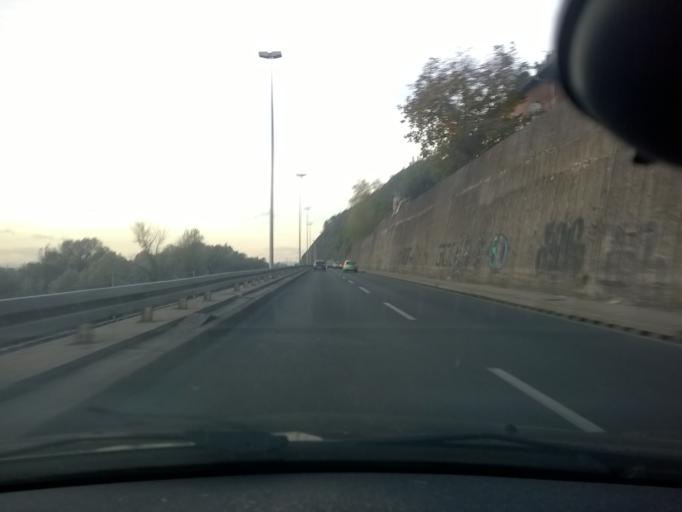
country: HR
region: Zagrebacka
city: Bestovje
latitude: 45.8238
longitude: 15.8276
